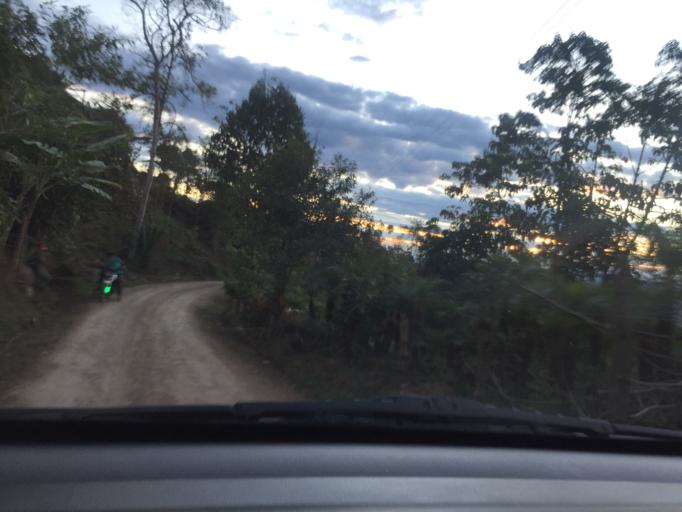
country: CO
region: Cundinamarca
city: Zipacon
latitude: 4.6991
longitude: -74.4101
